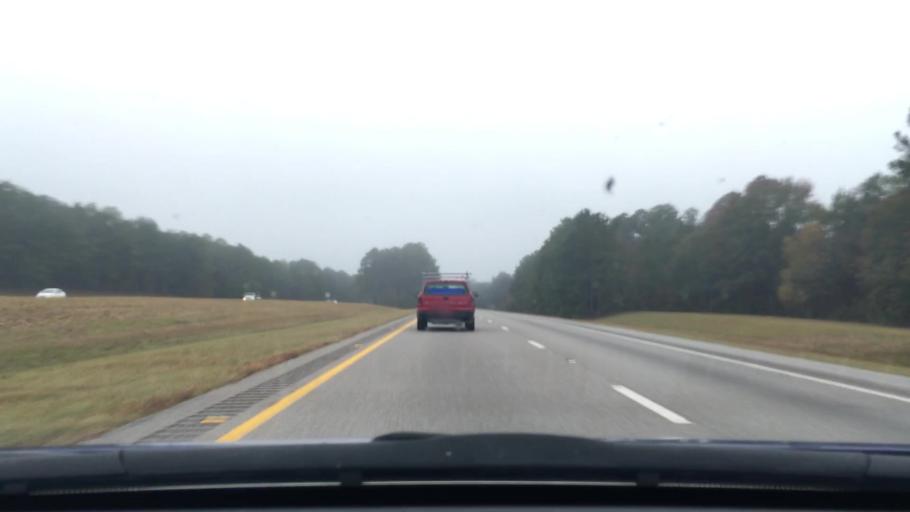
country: US
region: South Carolina
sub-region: Kershaw County
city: Camden
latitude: 34.2091
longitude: -80.4662
